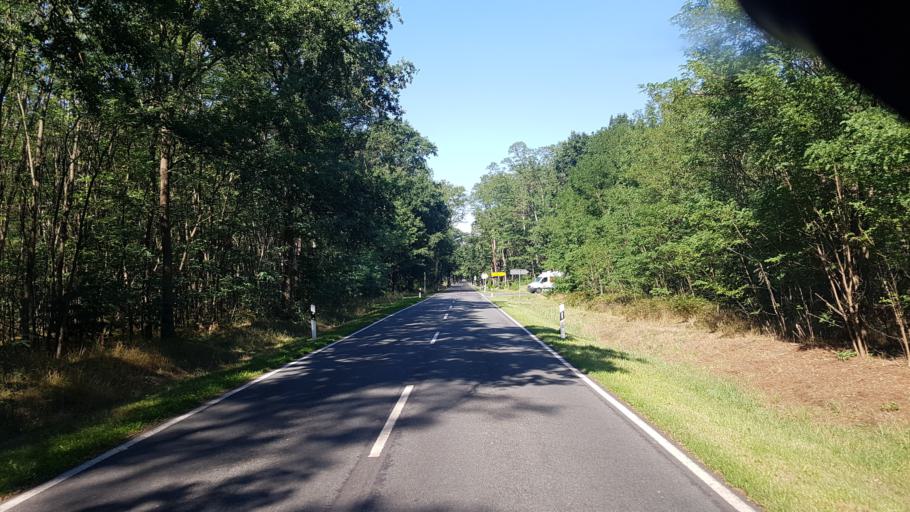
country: DE
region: Brandenburg
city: Altdobern
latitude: 51.6959
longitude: 14.0858
